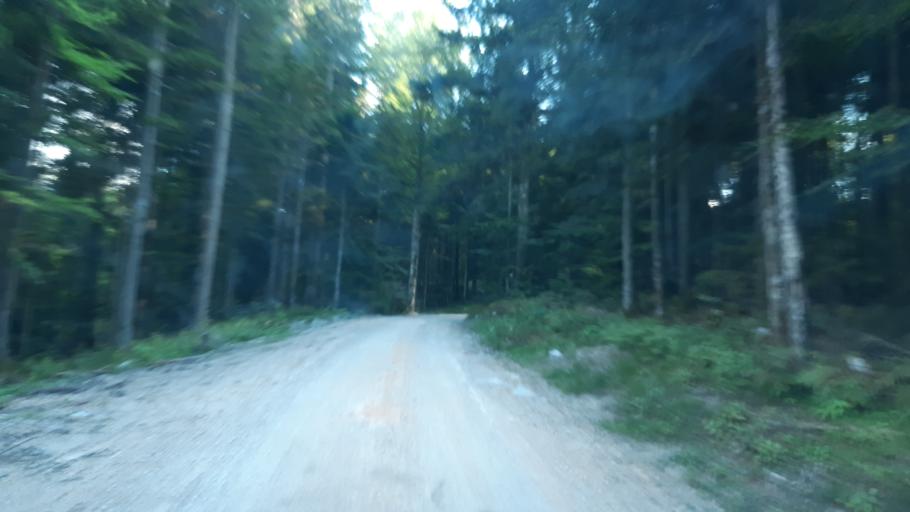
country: SI
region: Dolenjske Toplice
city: Dolenjske Toplice
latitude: 45.7096
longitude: 15.0105
